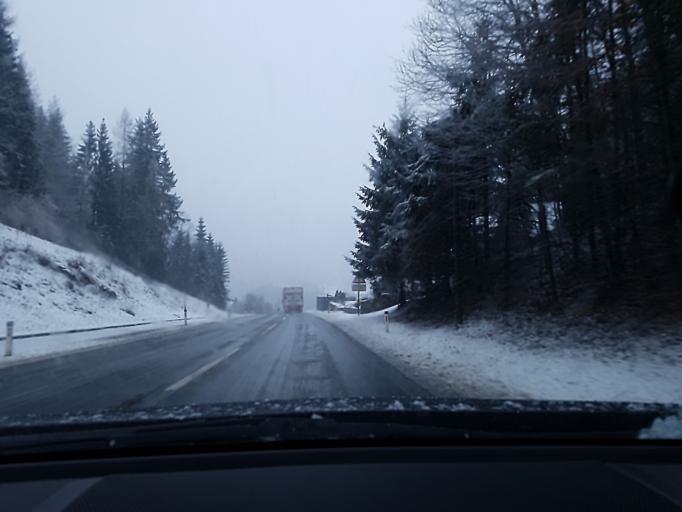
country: AT
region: Salzburg
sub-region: Politischer Bezirk Hallein
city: Scheffau am Tennengebirge
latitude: 47.5830
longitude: 13.2697
